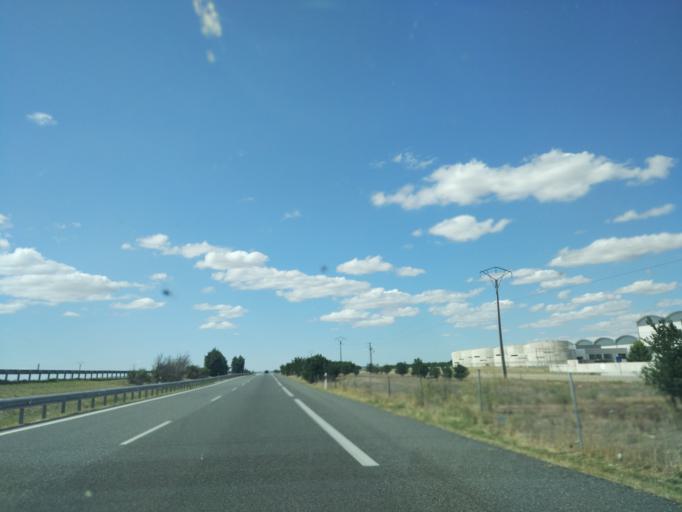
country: ES
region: Castille and Leon
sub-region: Provincia de Valladolid
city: San Vicente del Palacio
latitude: 41.2555
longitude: -4.8741
